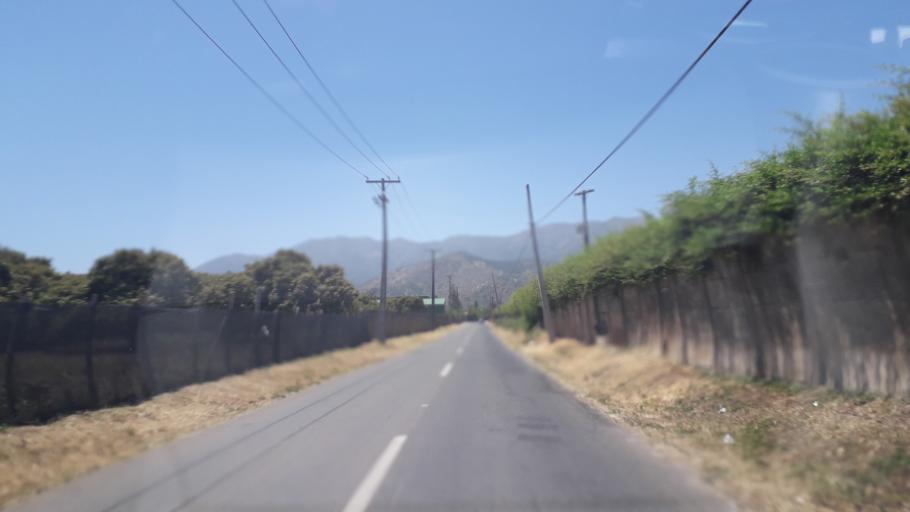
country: CL
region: Valparaiso
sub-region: Provincia de Quillota
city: Quillota
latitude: -32.9085
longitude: -71.2210
